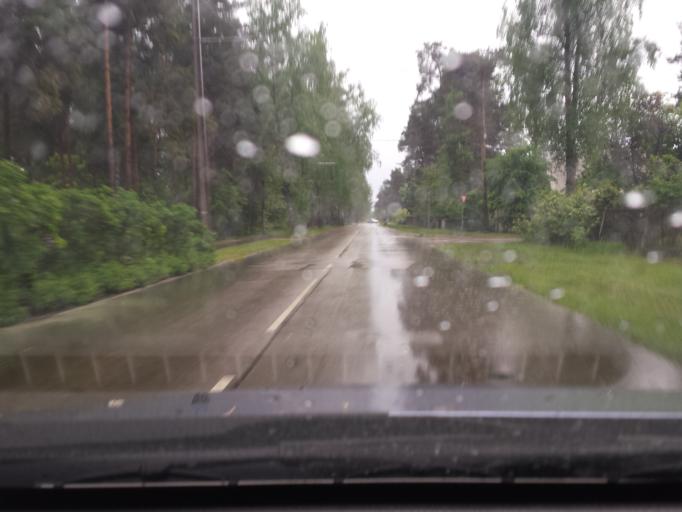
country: LV
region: Riga
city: Bolderaja
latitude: 57.0726
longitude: 24.1046
